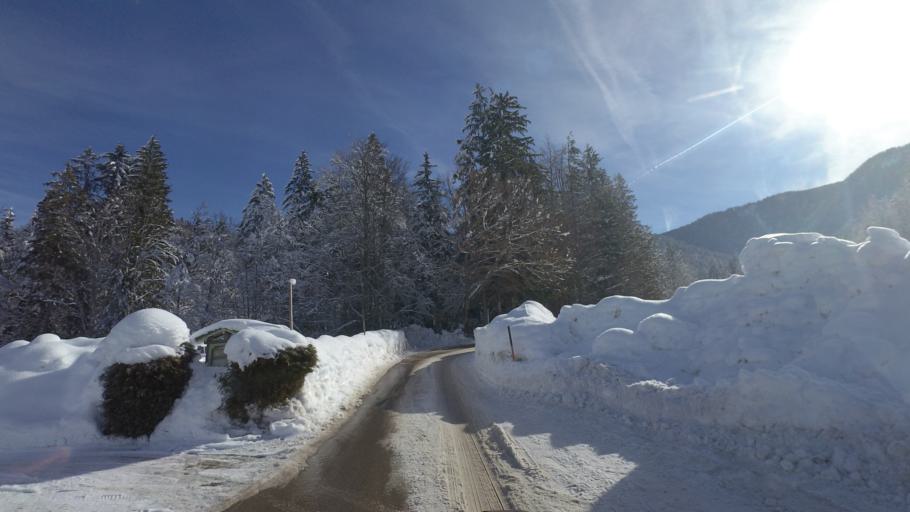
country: DE
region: Bavaria
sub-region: Upper Bavaria
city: Reit im Winkl
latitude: 47.6619
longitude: 12.4781
